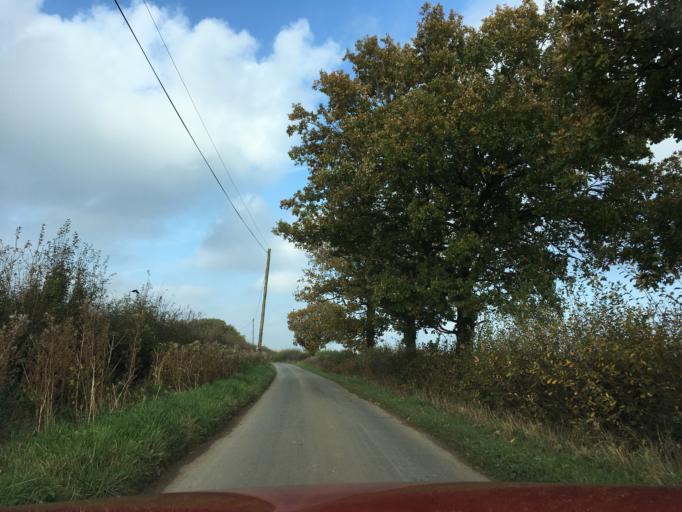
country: GB
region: England
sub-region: South Gloucestershire
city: Yate
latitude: 51.5718
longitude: -2.4255
